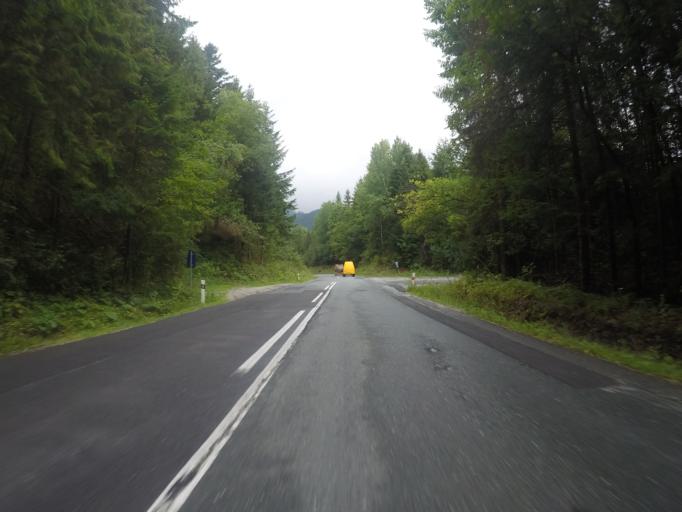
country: SK
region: Kosicky
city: Spisska Nova Ves
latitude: 48.8984
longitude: 20.5254
